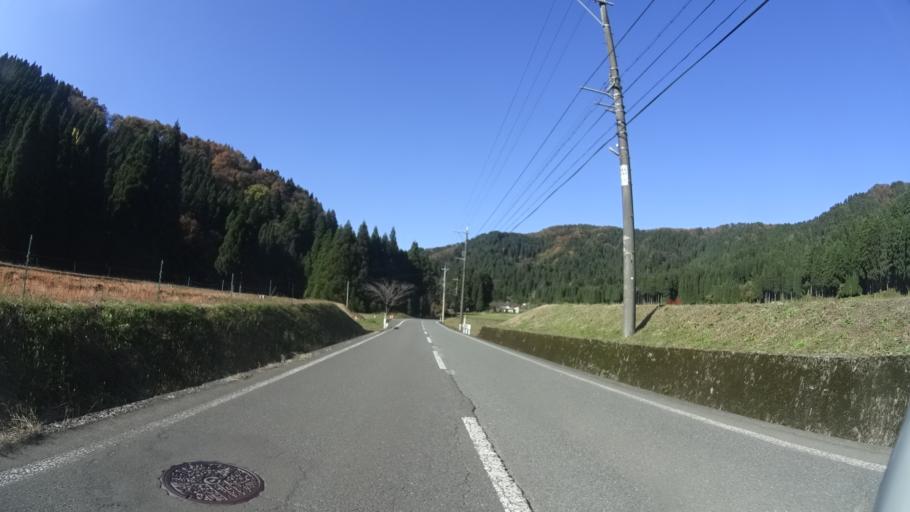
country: JP
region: Fukui
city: Ono
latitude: 35.8741
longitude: 136.3581
